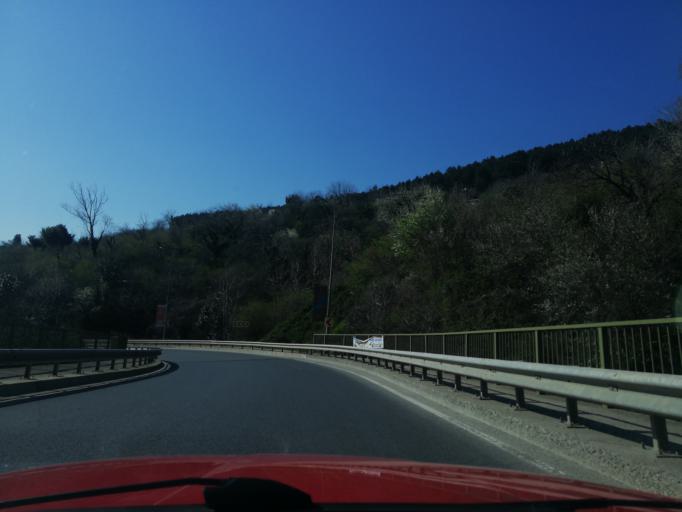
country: TR
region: Istanbul
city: Mahmut Sevket Pasa
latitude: 41.1231
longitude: 29.1320
